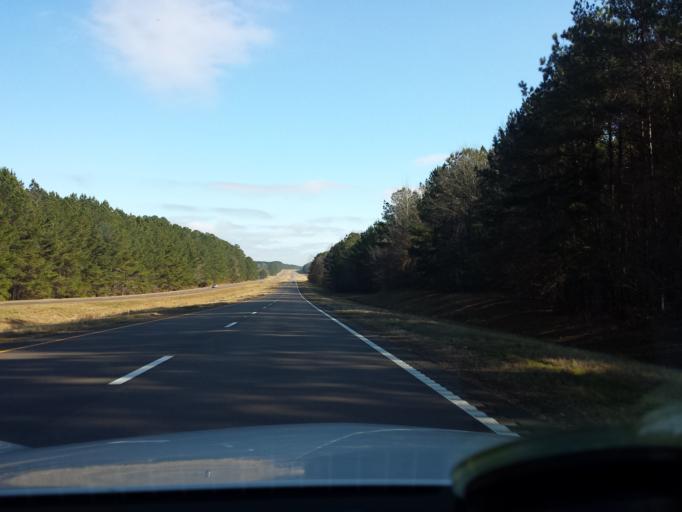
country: US
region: Mississippi
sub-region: Leake County
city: Carthage
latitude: 32.7544
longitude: -89.5897
